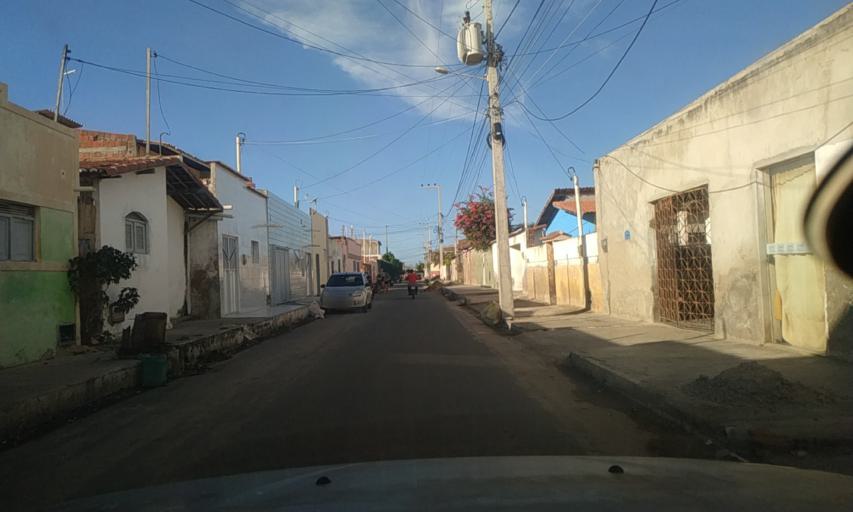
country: BR
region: Rio Grande do Norte
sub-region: Areia Branca
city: Areia Branca
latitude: -4.9523
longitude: -37.1260
